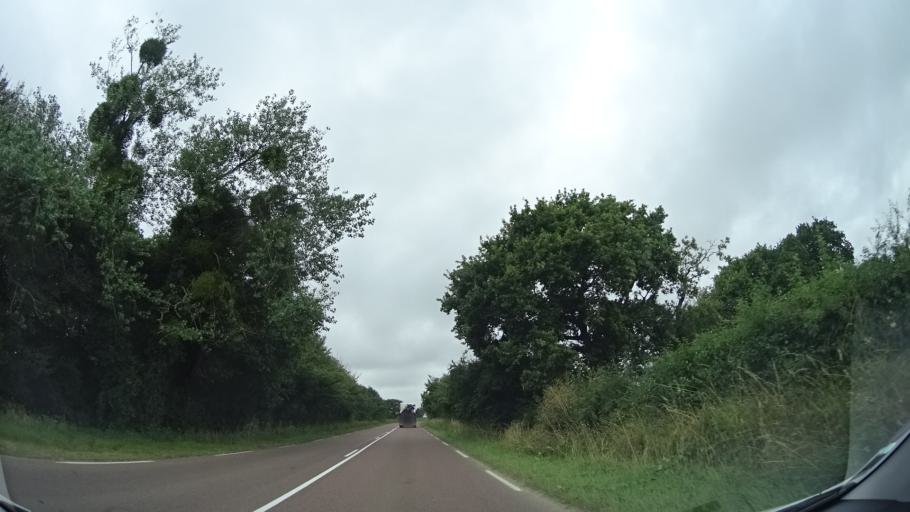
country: FR
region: Lower Normandy
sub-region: Departement de la Manche
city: Portbail
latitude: 49.3489
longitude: -1.6654
